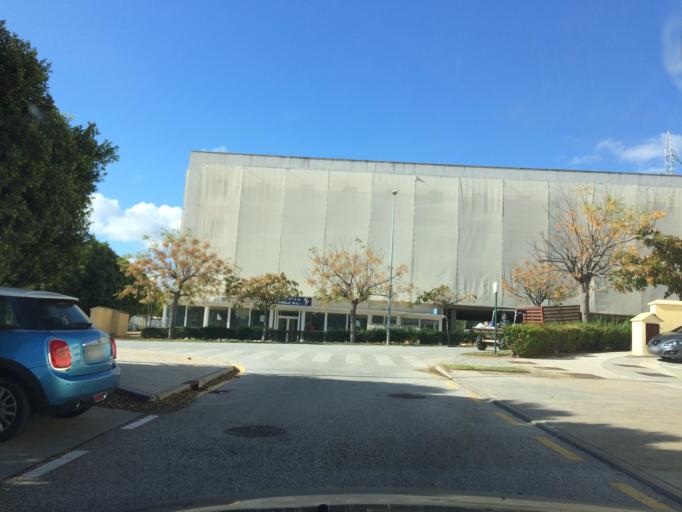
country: ES
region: Andalusia
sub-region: Provincia de Malaga
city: Estacion de Cartama
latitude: 36.7328
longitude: -4.5469
